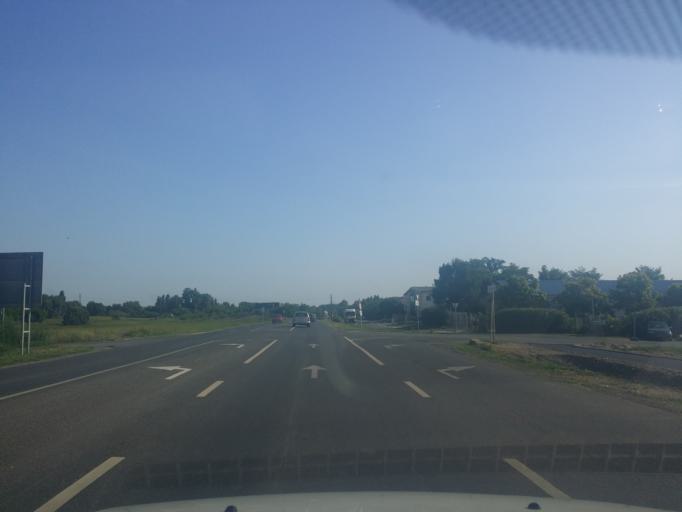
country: HU
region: Bacs-Kiskun
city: Baja
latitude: 46.1817
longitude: 18.9772
